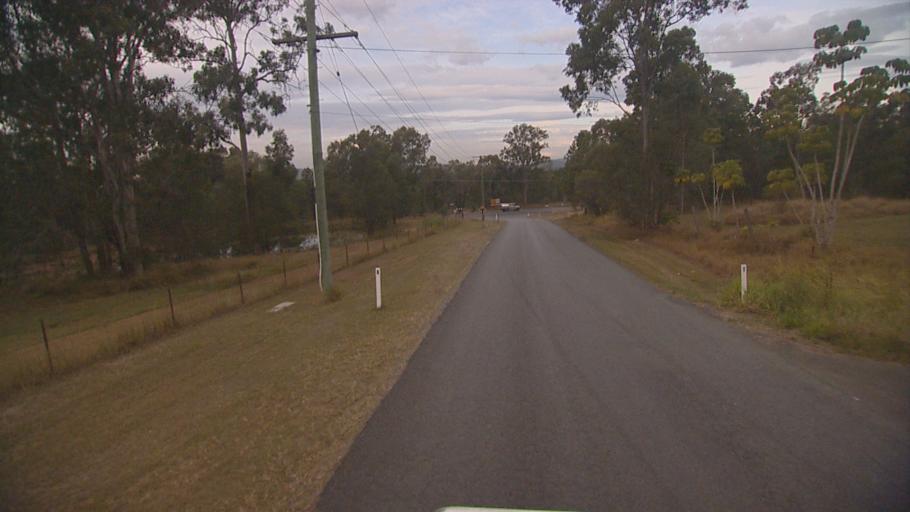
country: AU
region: Queensland
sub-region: Logan
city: Chambers Flat
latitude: -27.8195
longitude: 153.0979
